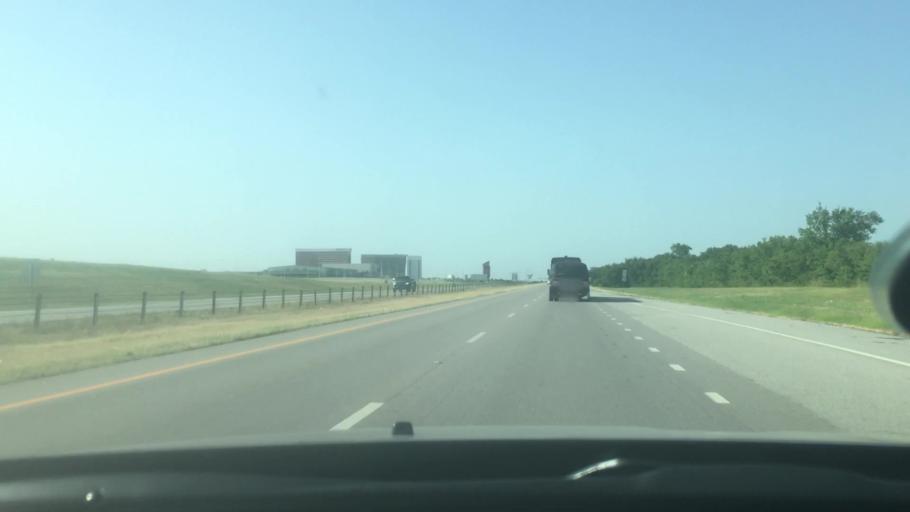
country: US
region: Oklahoma
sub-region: Bryan County
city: Calera
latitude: 33.9644
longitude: -96.4168
